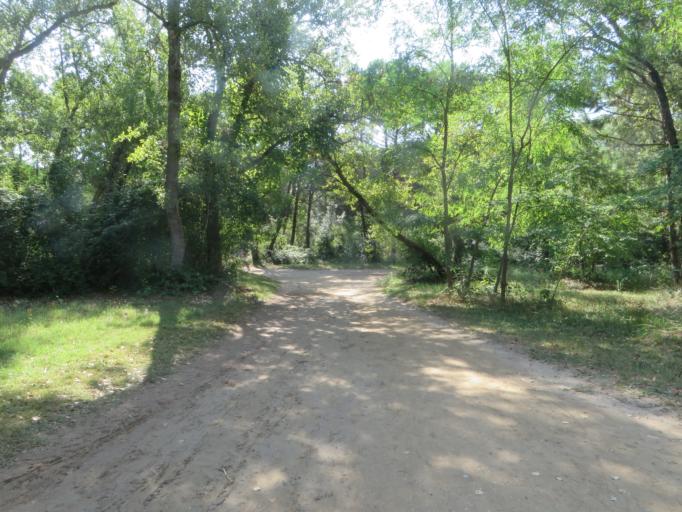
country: IT
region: Veneto
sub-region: Provincia di Venezia
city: Bibione
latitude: 45.6239
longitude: 12.9593
